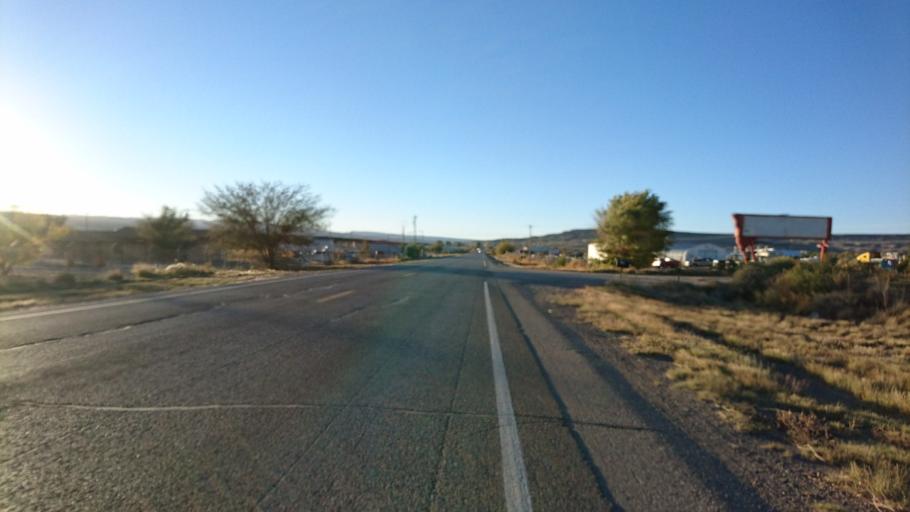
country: US
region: New Mexico
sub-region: Cibola County
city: Grants
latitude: 35.1359
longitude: -107.8208
